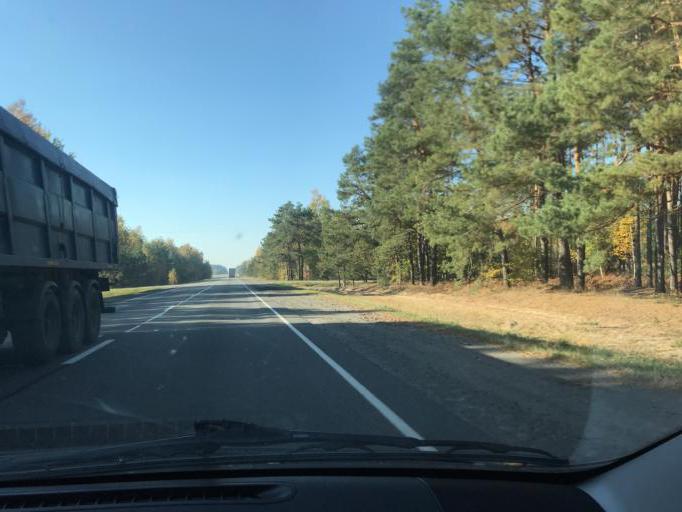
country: BY
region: Brest
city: Davyd-Haradok
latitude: 52.2456
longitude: 27.1263
